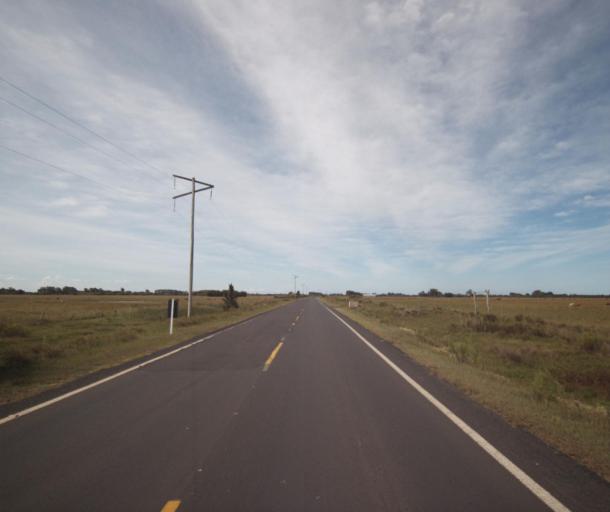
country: BR
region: Rio Grande do Sul
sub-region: Rio Grande
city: Rio Grande
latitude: -31.9309
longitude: -51.9615
